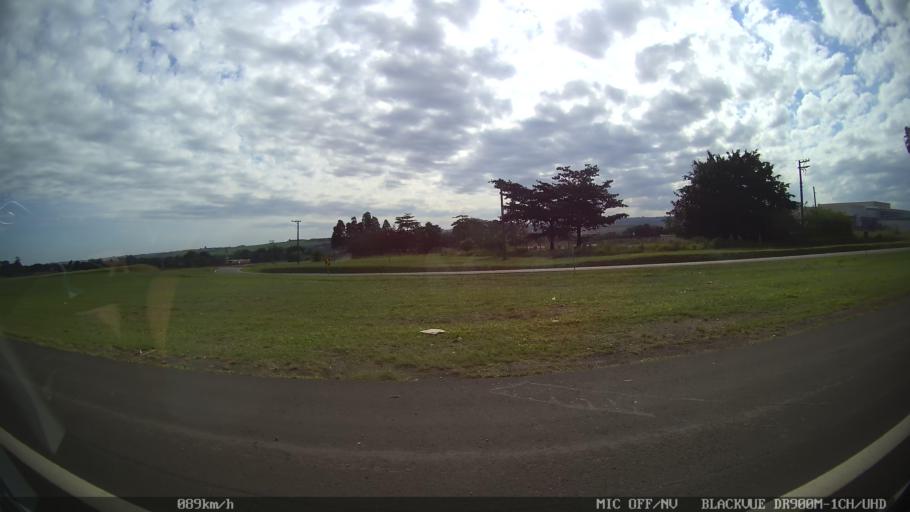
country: BR
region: Sao Paulo
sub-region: Limeira
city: Limeira
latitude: -22.5826
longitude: -47.4550
